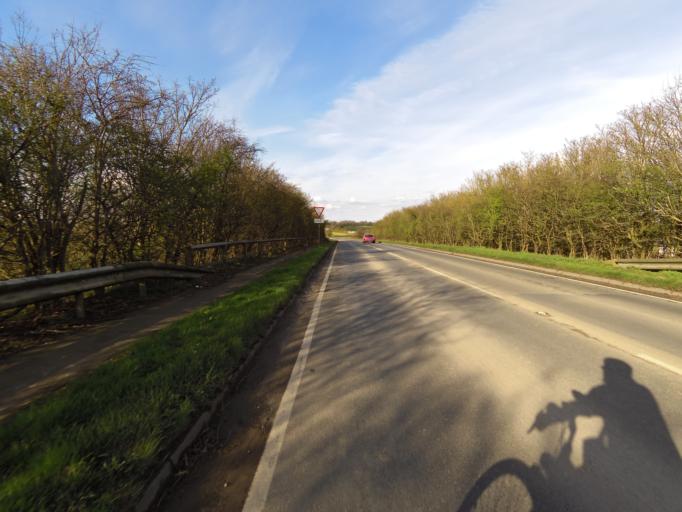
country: GB
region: England
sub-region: East Riding of Yorkshire
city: Pollington
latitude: 53.6815
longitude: -1.0558
